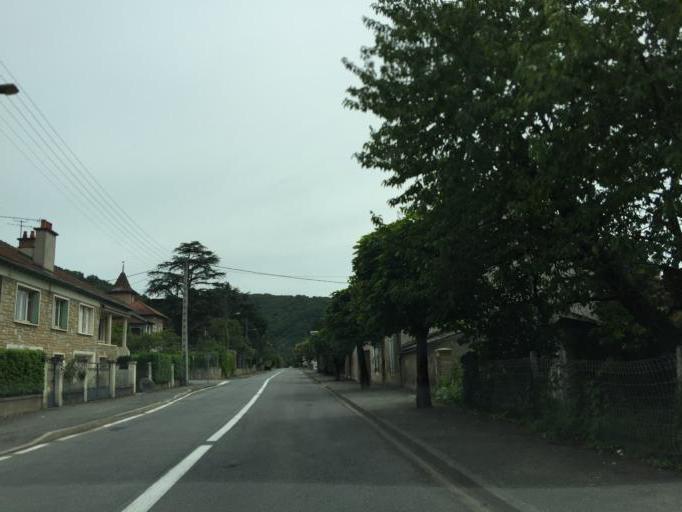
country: FR
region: Midi-Pyrenees
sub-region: Departement de l'Aveyron
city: Villefranche-de-Rouergue
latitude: 44.3424
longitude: 2.0322
